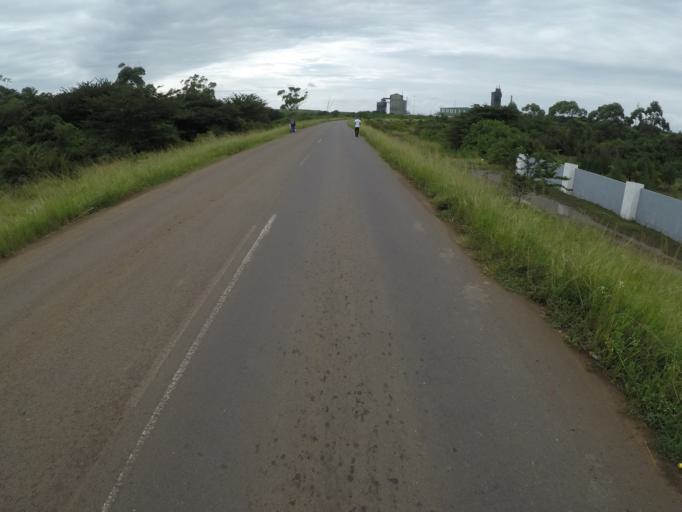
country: ZA
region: KwaZulu-Natal
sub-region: uThungulu District Municipality
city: Empangeni
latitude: -28.7157
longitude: 31.8664
